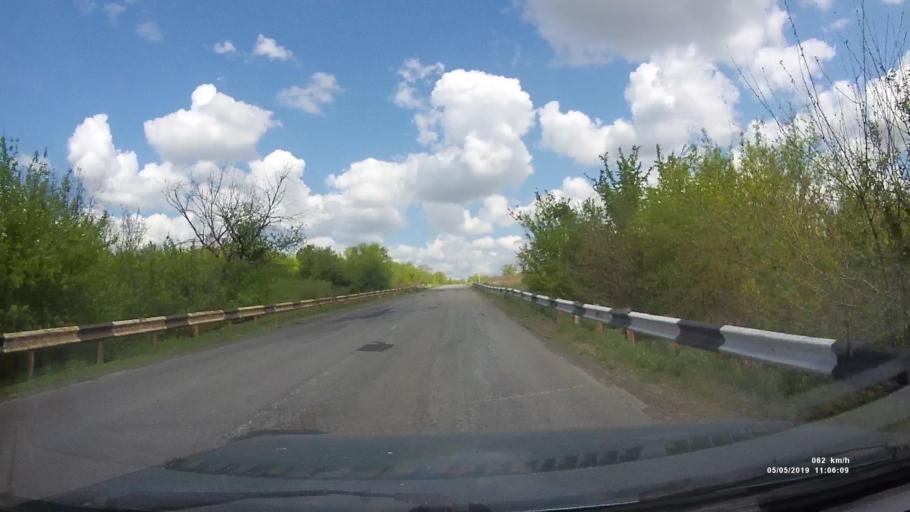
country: RU
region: Rostov
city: Ust'-Donetskiy
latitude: 47.7127
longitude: 40.9111
